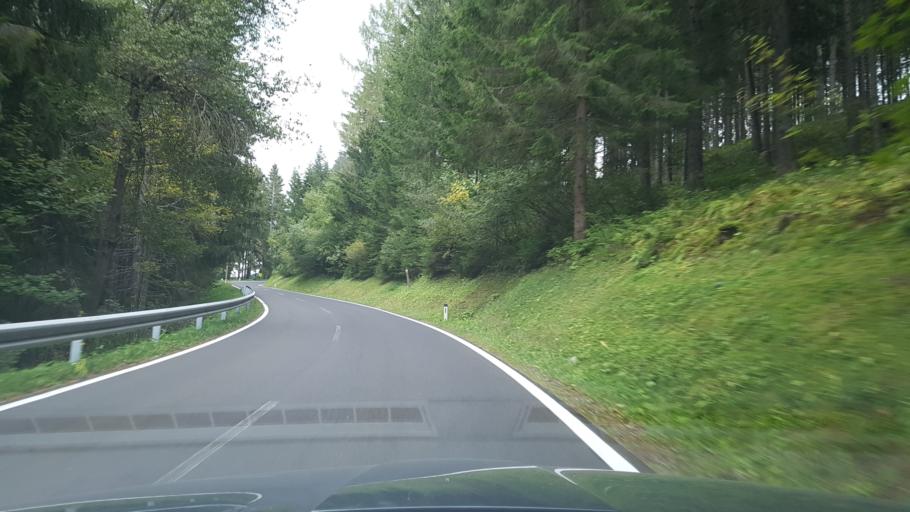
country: AT
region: Styria
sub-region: Politischer Bezirk Murtal
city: Kleinlobming
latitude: 47.1327
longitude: 14.8690
